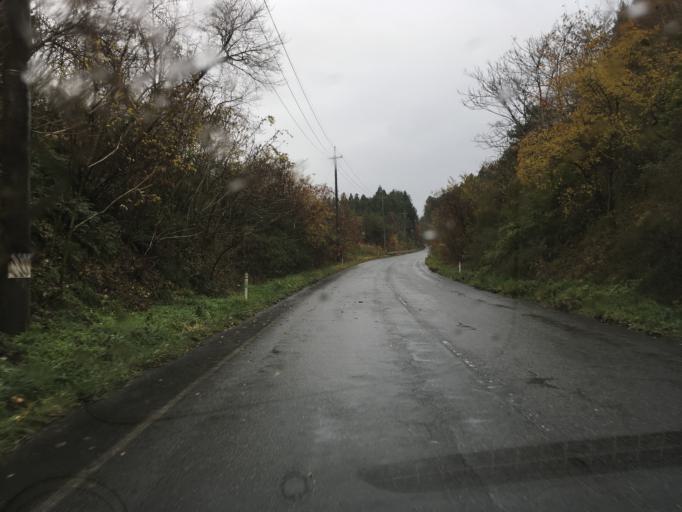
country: JP
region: Iwate
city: Ichinoseki
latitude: 38.7941
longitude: 141.2420
